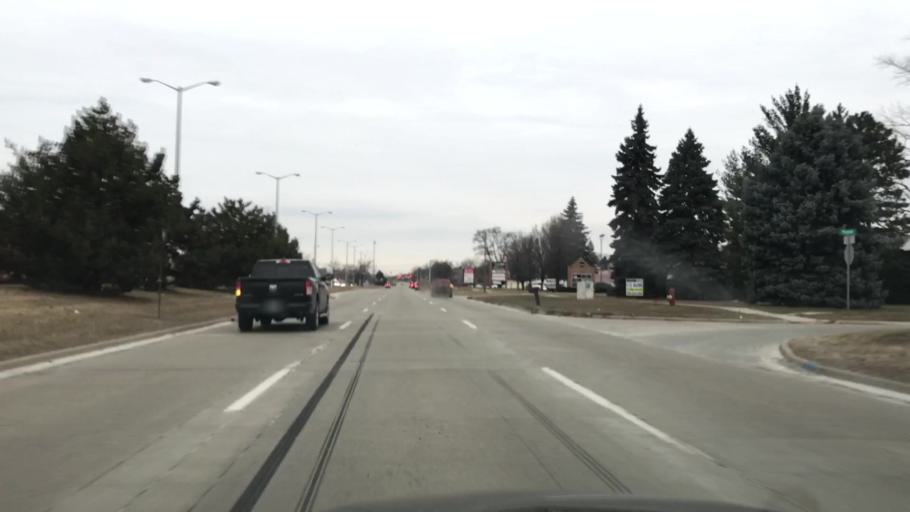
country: US
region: Michigan
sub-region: Macomb County
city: Utica
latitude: 42.6159
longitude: -83.0515
